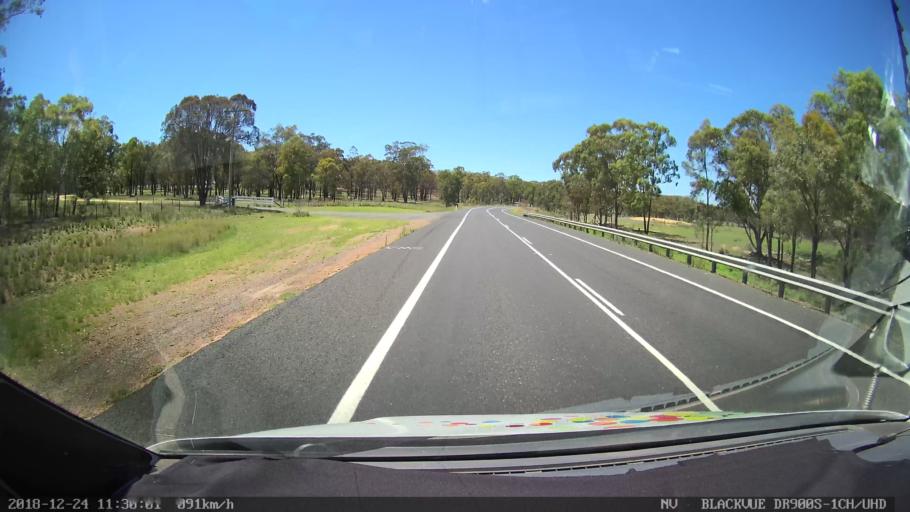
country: AU
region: New South Wales
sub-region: Upper Hunter Shire
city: Merriwa
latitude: -32.1996
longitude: 150.4666
